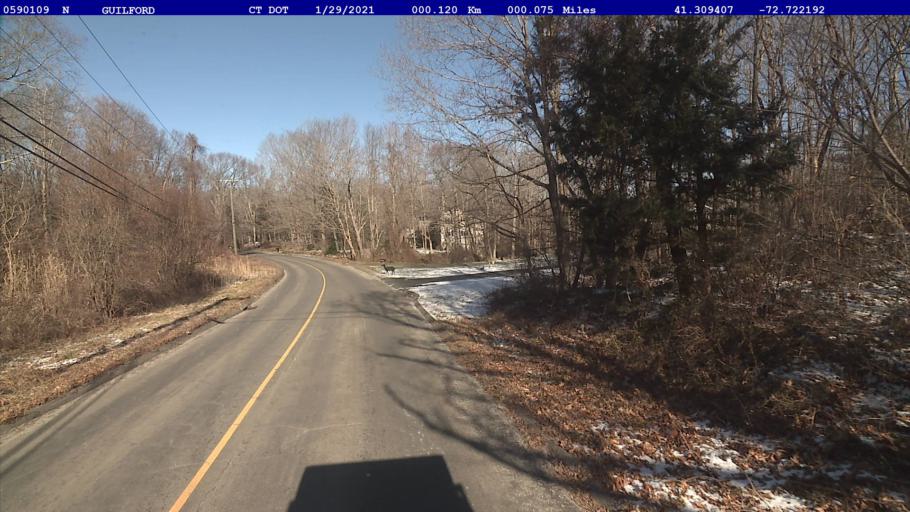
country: US
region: Connecticut
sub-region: New Haven County
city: Guilford
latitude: 41.3094
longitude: -72.7222
